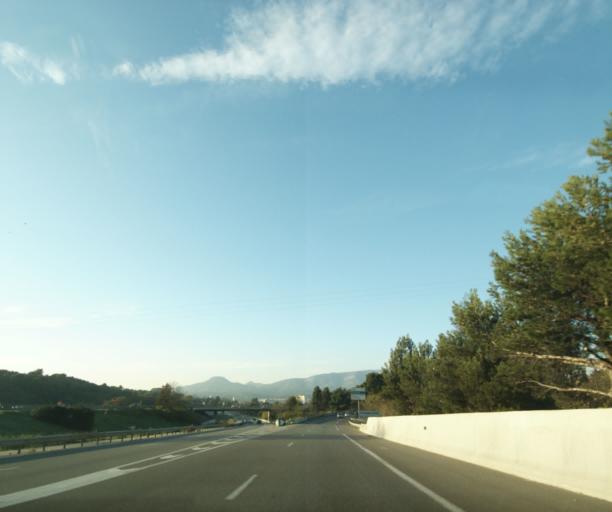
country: FR
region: Provence-Alpes-Cote d'Azur
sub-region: Departement des Bouches-du-Rhone
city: Aubagne
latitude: 43.2786
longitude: 5.5860
